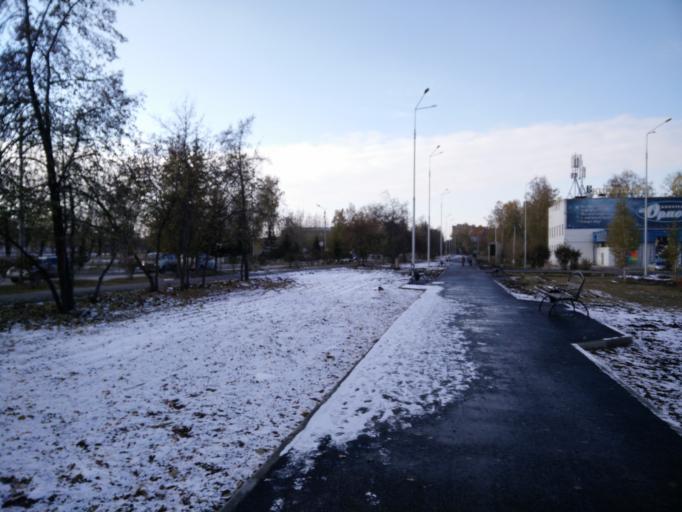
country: RU
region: Novosibirsk
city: Berdsk
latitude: 54.7560
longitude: 83.1044
